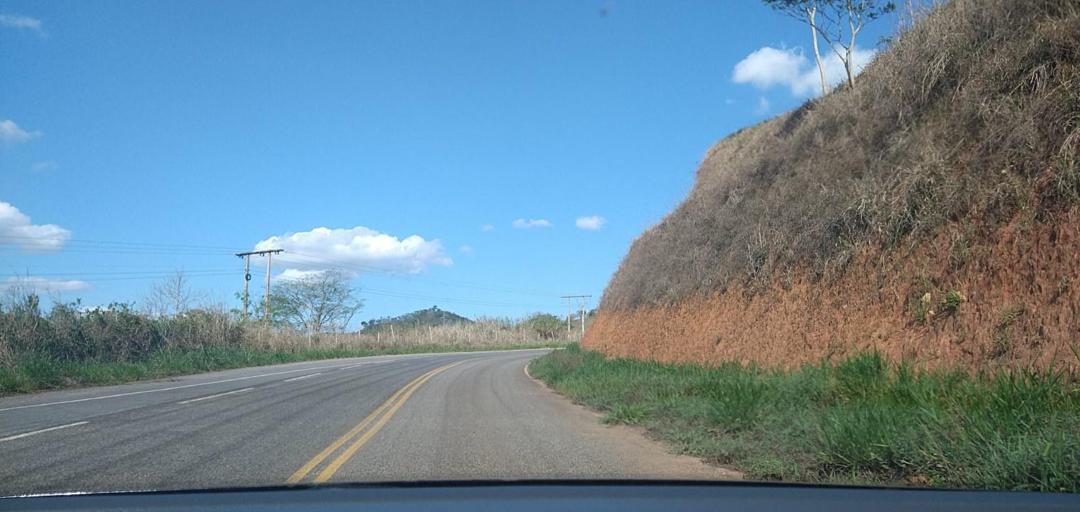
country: BR
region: Minas Gerais
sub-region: Alvinopolis
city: Alvinopolis
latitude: -20.1683
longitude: -42.9226
